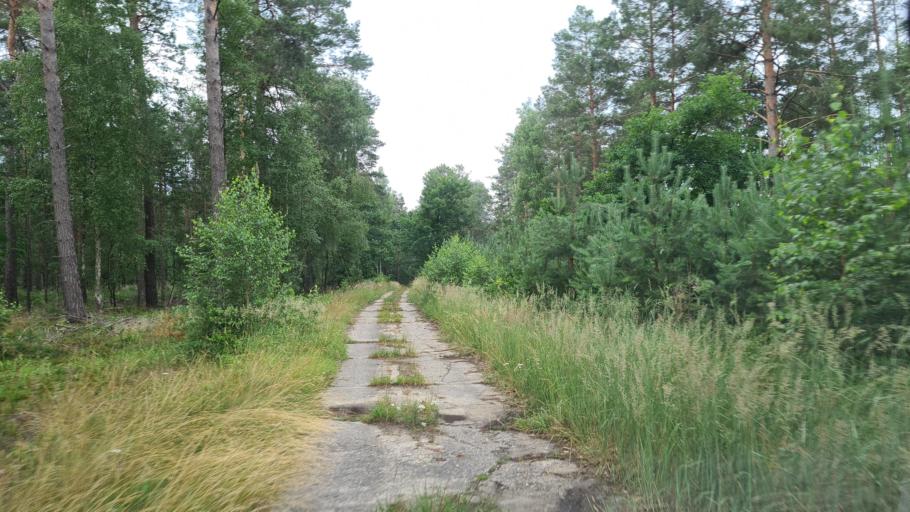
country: DE
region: Brandenburg
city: Crinitz
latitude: 51.7204
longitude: 13.7269
